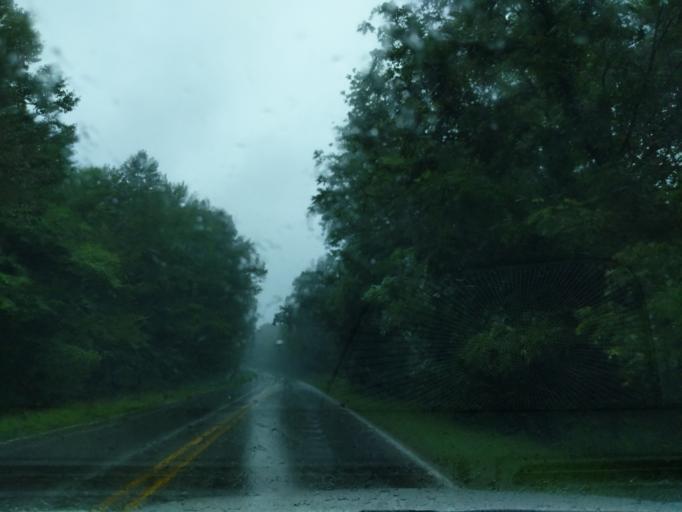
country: US
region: Kentucky
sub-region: Barren County
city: Cave City
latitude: 37.1459
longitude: -86.0894
